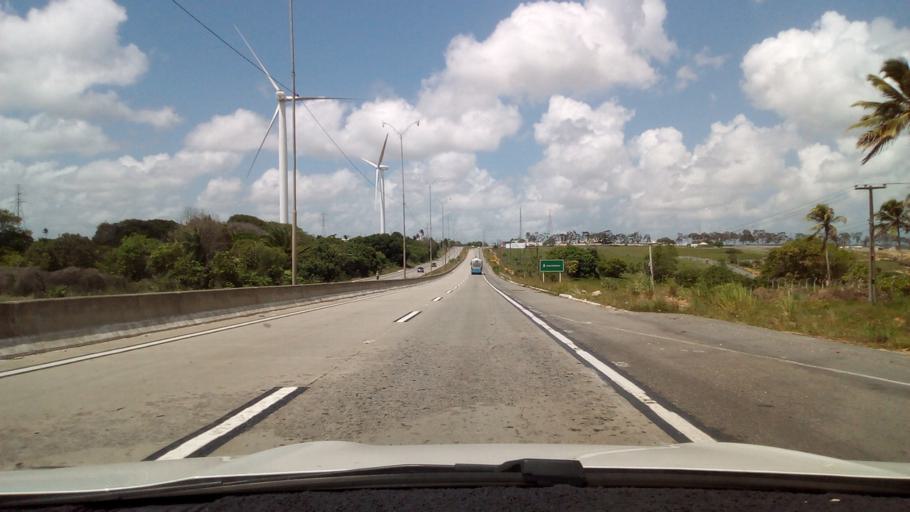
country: BR
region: Paraiba
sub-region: Conde
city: Conde
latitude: -7.2700
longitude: -34.9374
